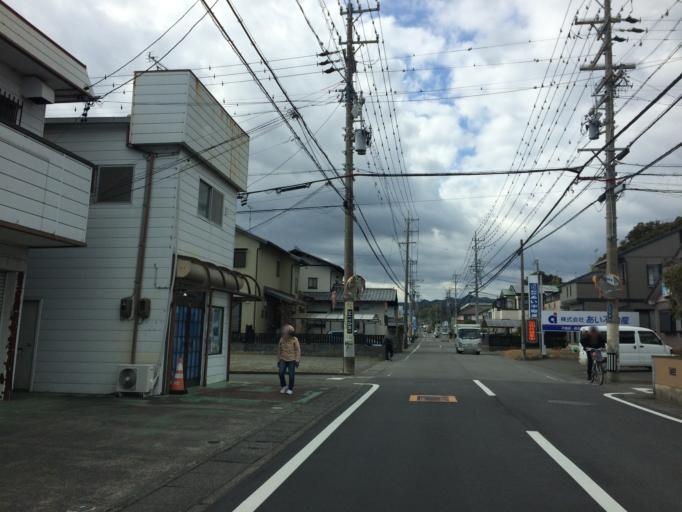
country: JP
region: Shizuoka
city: Fujieda
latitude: 34.8641
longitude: 138.2457
